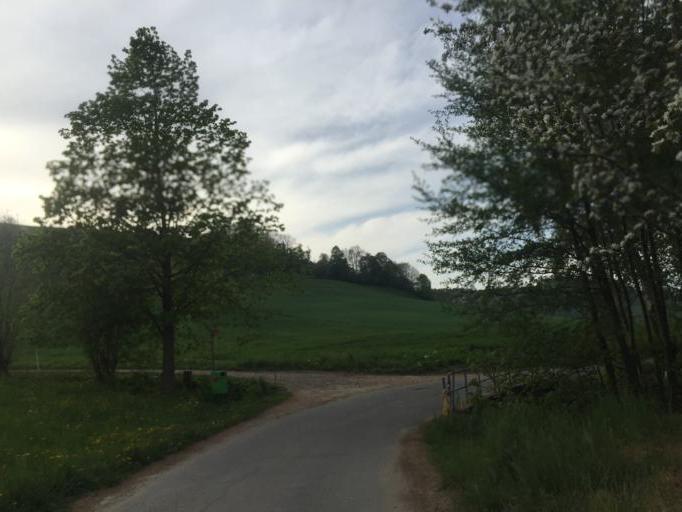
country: CH
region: Bern
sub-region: Bern-Mittelland District
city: Munsingen
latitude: 46.8586
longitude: 7.5465
